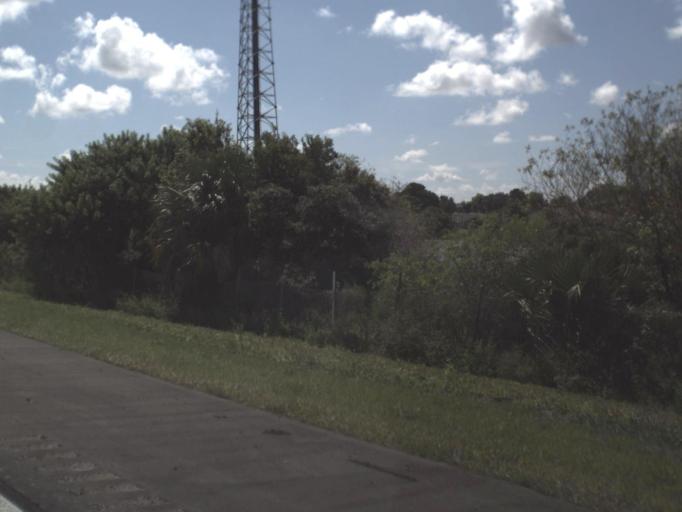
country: US
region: Florida
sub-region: Lee County
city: Suncoast Estates
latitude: 26.7237
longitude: -81.8293
